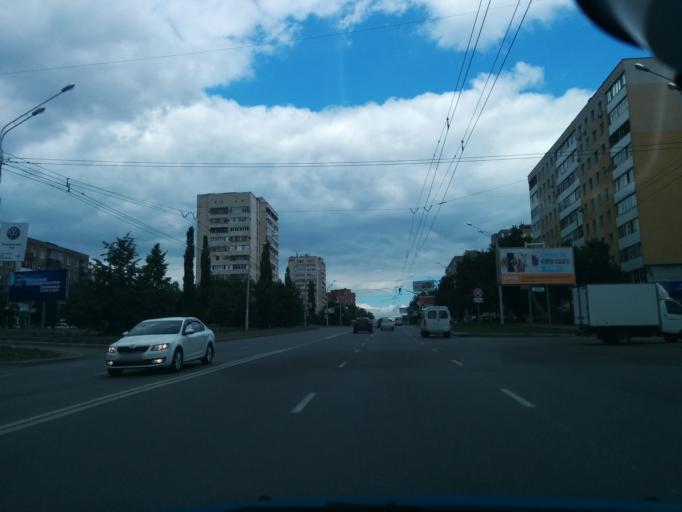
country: RU
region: Bashkortostan
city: Ufa
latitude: 54.7280
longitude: 55.9773
